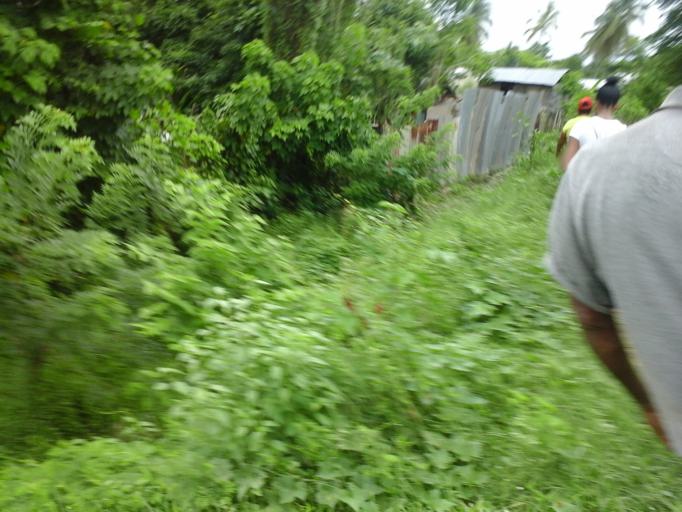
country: CO
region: Bolivar
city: San Pablo
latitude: 10.1458
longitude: -75.2763
